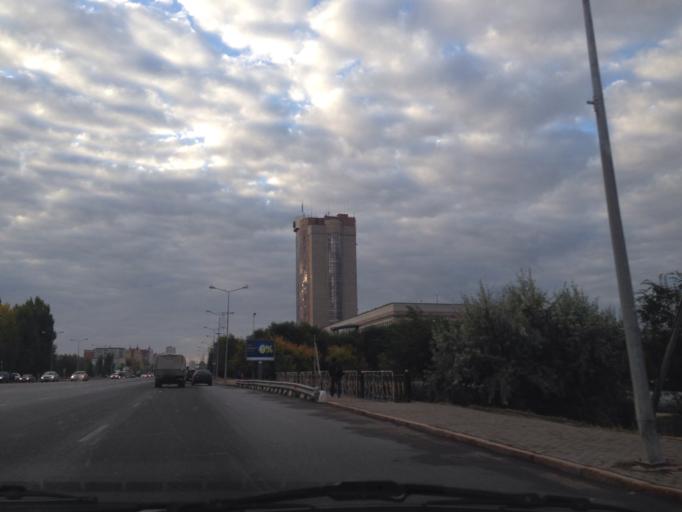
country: KZ
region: Astana Qalasy
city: Astana
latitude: 51.1545
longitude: 71.4537
